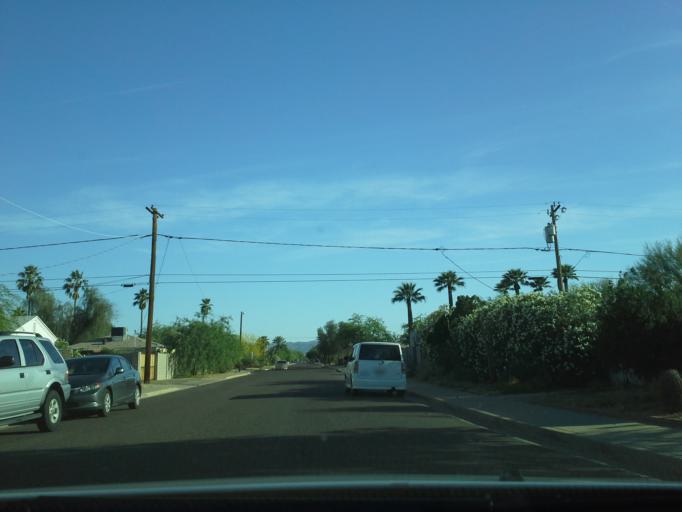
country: US
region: Arizona
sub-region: Maricopa County
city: Phoenix
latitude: 33.4703
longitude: -112.0521
